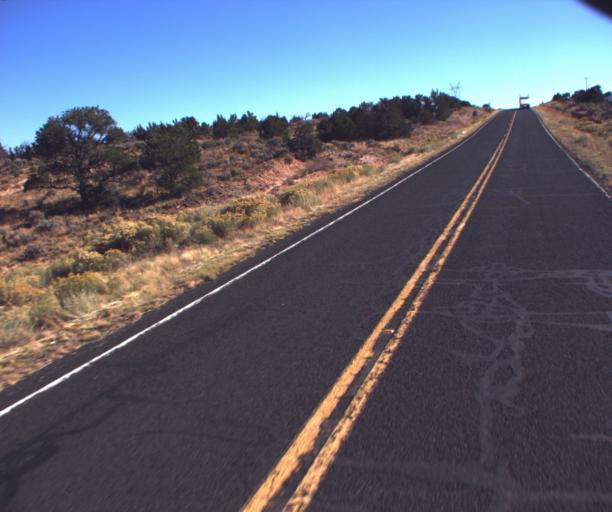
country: US
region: Arizona
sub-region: Apache County
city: Ganado
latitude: 35.6447
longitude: -109.5467
